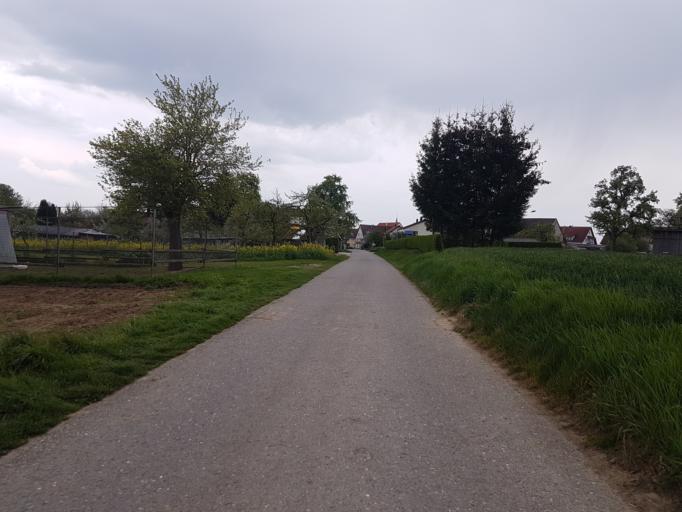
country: DE
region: Baden-Wuerttemberg
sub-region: Regierungsbezirk Stuttgart
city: Bondorf
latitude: 48.4984
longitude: 8.8065
